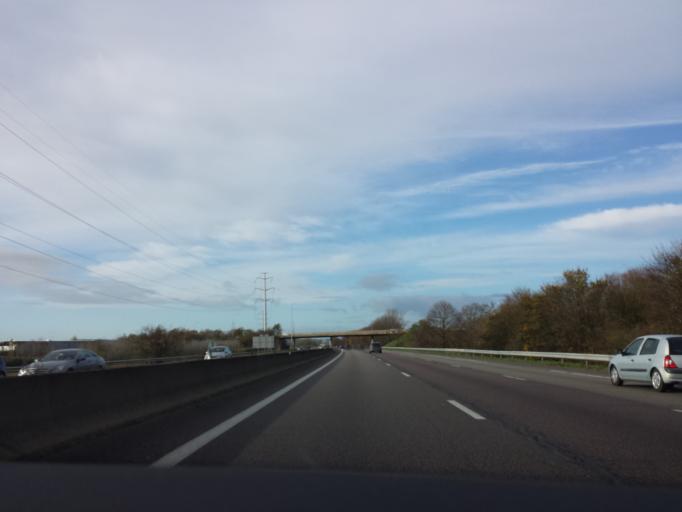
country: FR
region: Ile-de-France
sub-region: Departement des Yvelines
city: Flins-sur-Seine
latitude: 48.9706
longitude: 1.8798
